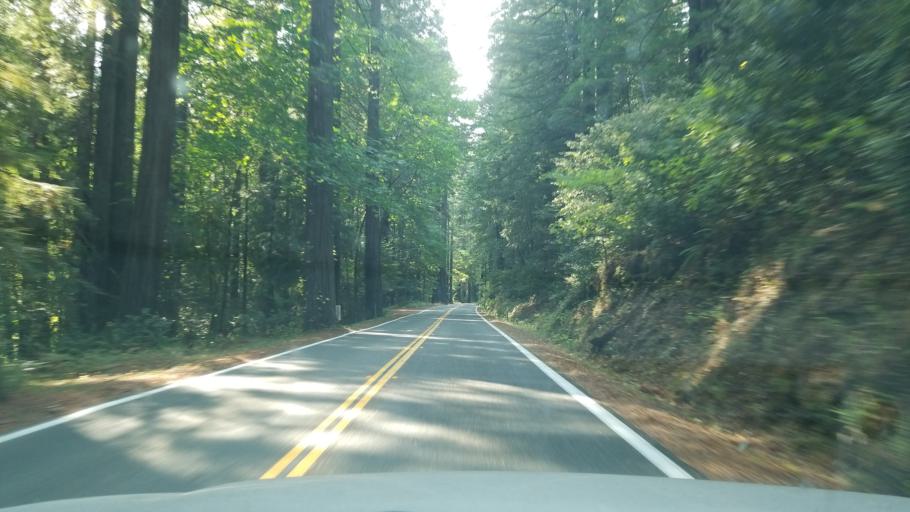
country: US
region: California
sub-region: Humboldt County
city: Redway
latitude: 40.2585
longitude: -123.8376
